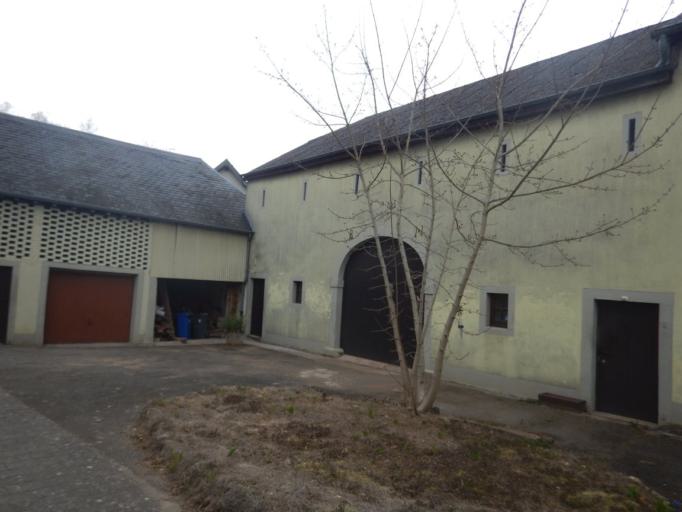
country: LU
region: Diekirch
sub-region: Canton de Redange
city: Ell
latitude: 49.7861
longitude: 5.8561
